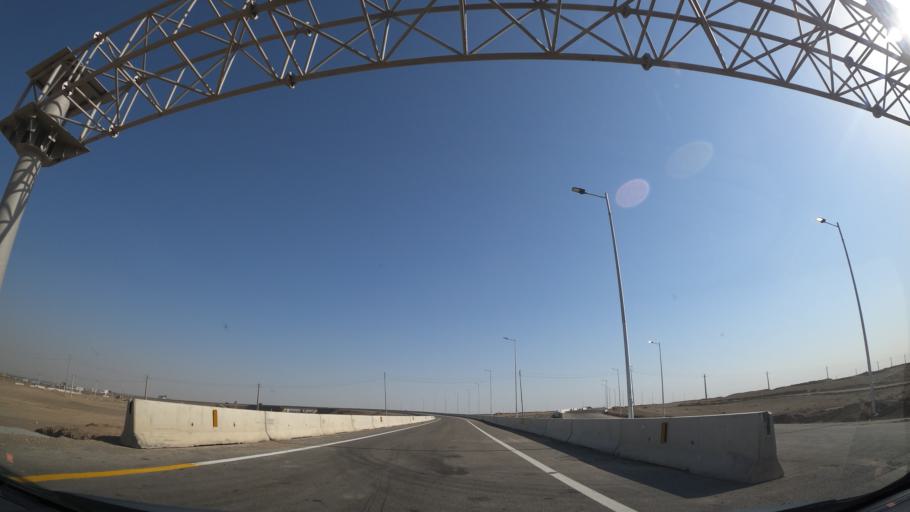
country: IR
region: Tehran
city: Eqbaliyeh
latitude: 35.1358
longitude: 51.5079
